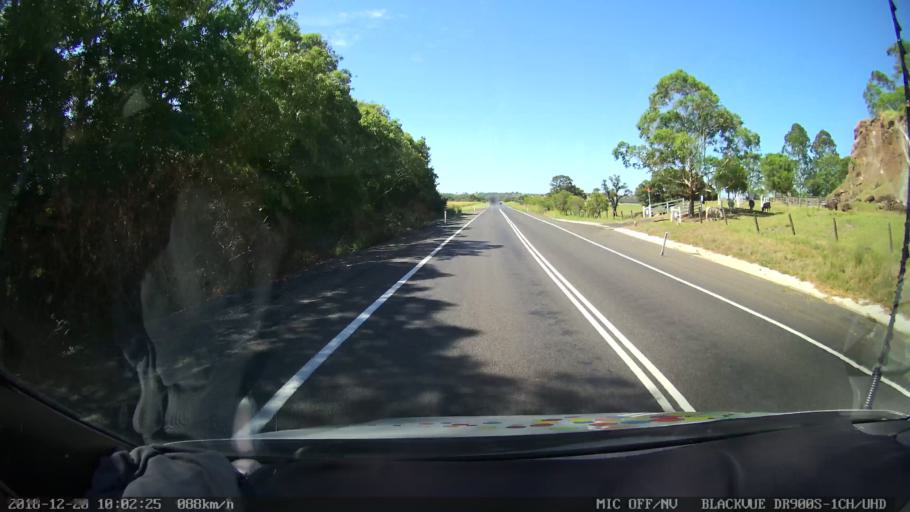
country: AU
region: New South Wales
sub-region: Lismore Municipality
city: East Lismore
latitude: -28.8577
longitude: 153.2613
